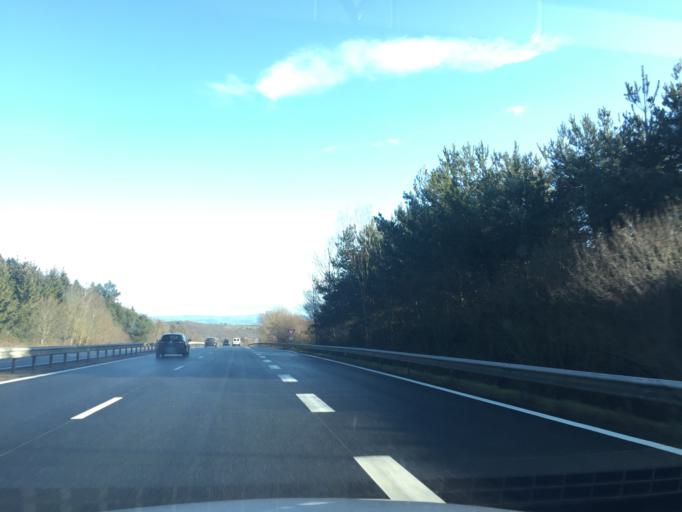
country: FR
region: Rhone-Alpes
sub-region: Departement de la Loire
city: Saint-Germain-Laval
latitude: 45.8703
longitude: 3.9321
